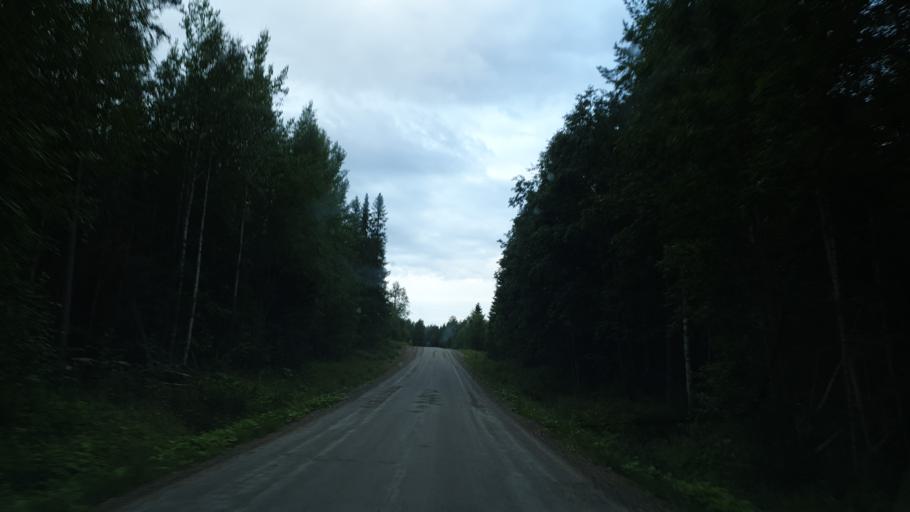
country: FI
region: Kainuu
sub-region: Kehys-Kainuu
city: Kuhmo
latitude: 64.2028
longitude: 29.3721
